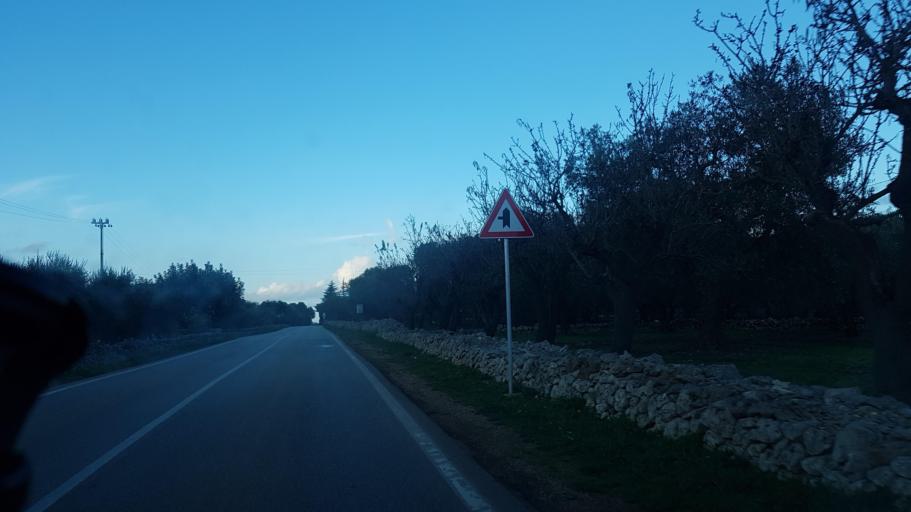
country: IT
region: Apulia
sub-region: Provincia di Brindisi
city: San Michele Salentino
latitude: 40.6618
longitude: 17.6003
